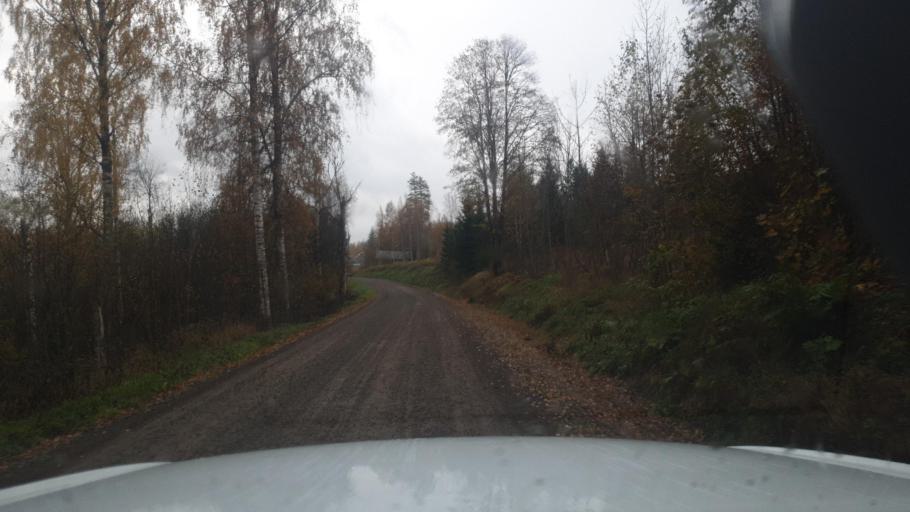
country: SE
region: Vaermland
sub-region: Torsby Kommun
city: Torsby
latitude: 59.9743
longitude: 12.8579
